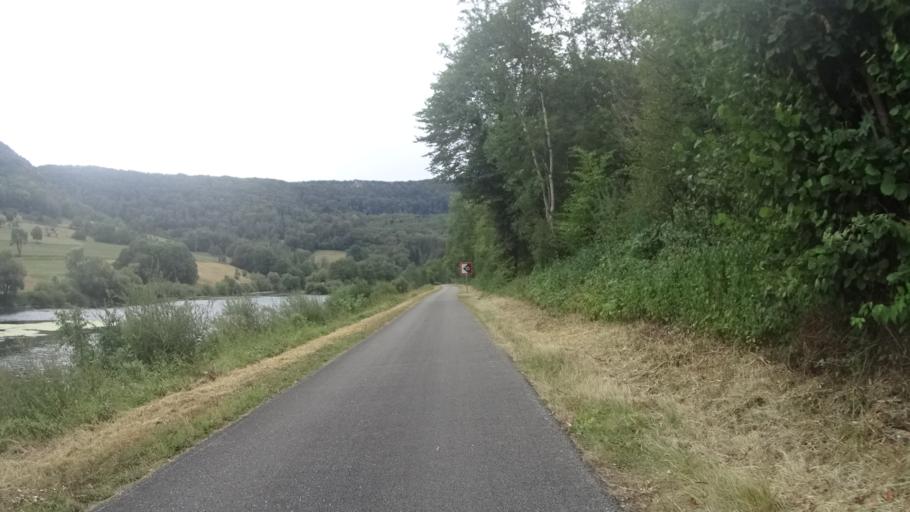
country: FR
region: Franche-Comte
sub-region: Departement du Doubs
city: Baume-les-Dames
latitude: 47.3361
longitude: 6.3143
